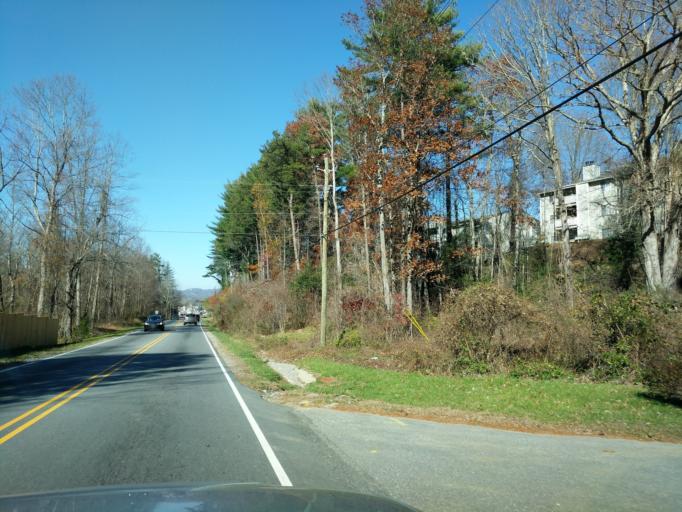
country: US
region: North Carolina
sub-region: Buncombe County
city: Biltmore Forest
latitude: 35.5295
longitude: -82.5179
